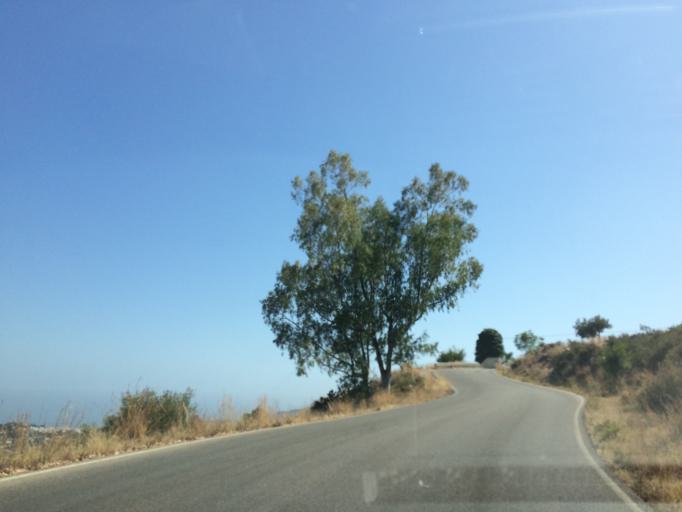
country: ES
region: Andalusia
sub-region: Provincia de Malaga
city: Frigiliana
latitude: 36.7973
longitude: -3.9028
